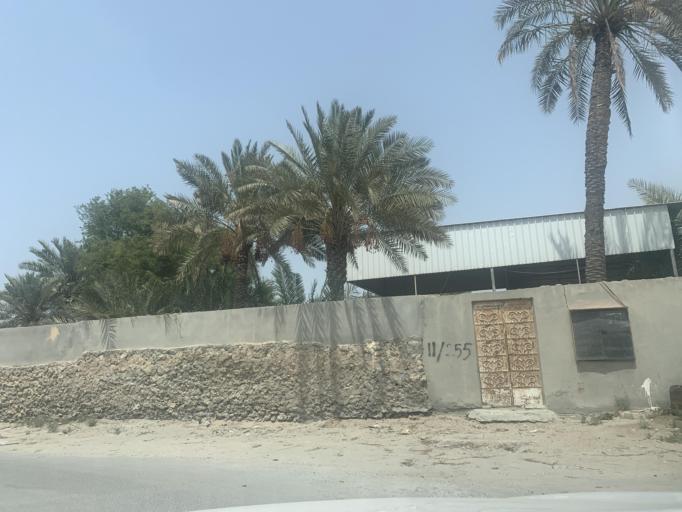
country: BH
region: Manama
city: Jidd Hafs
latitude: 26.2201
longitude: 50.4653
